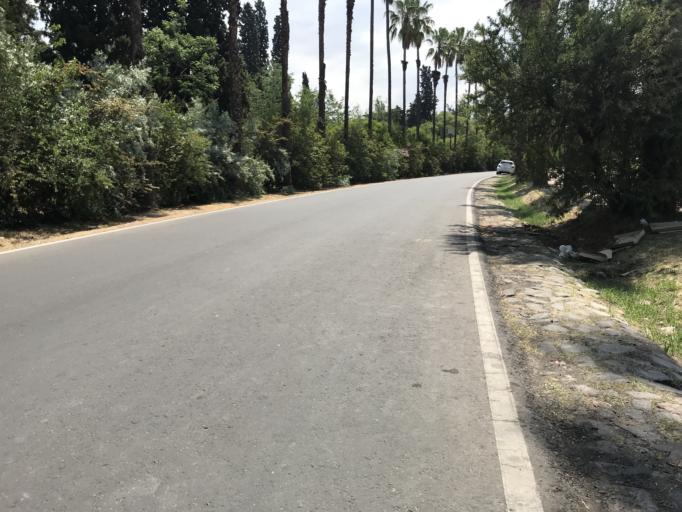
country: AR
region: Mendoza
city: Mendoza
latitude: -32.8941
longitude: -68.8699
